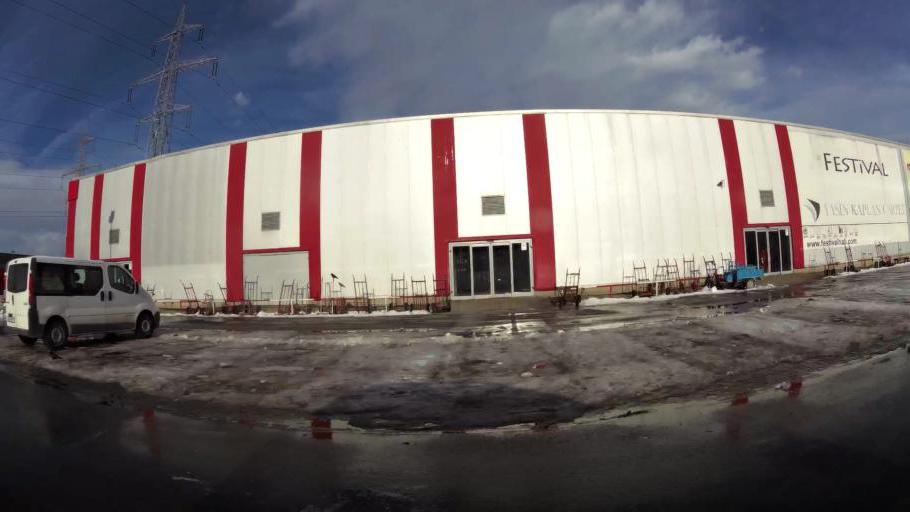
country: RO
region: Ilfov
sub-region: Voluntari City
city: Voluntari
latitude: 44.4755
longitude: 26.1820
